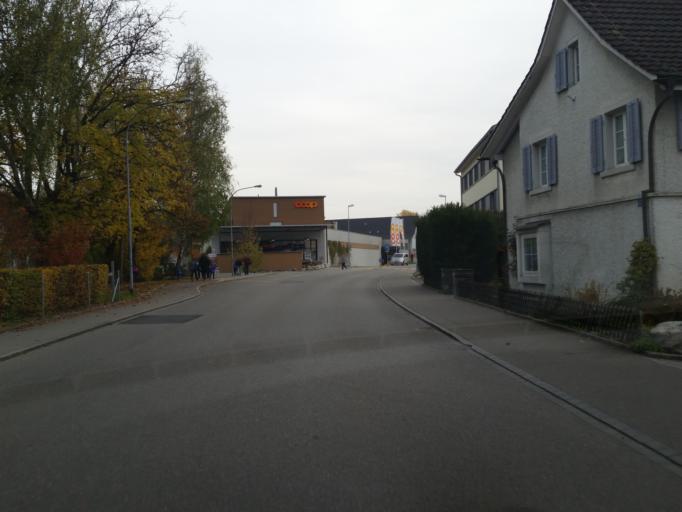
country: CH
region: Zurich
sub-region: Bezirk Winterthur
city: Neftenbach / Dorf Neftenbach
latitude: 47.5274
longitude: 8.6685
